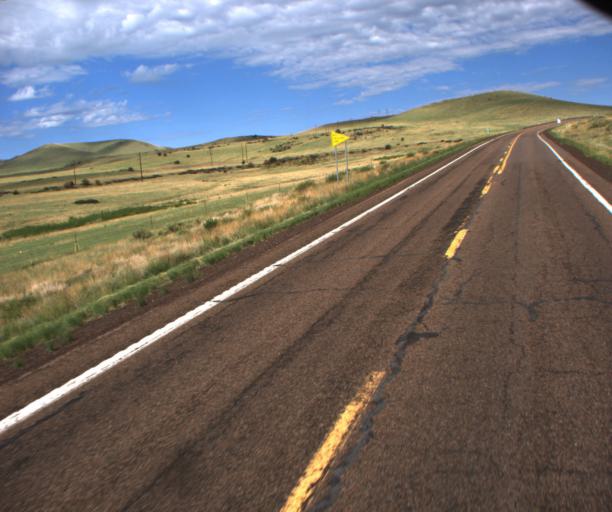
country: US
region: Arizona
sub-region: Apache County
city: Springerville
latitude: 34.2067
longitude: -109.4199
